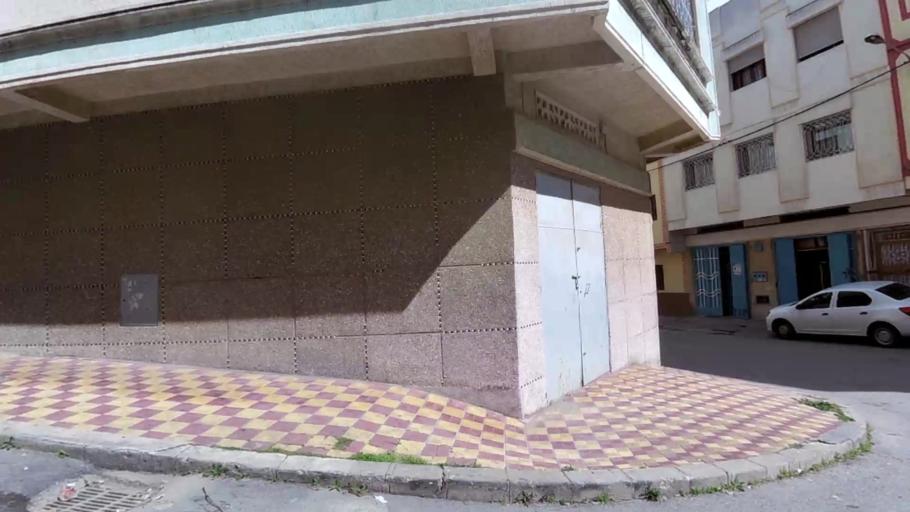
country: MA
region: Tanger-Tetouan
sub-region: Tanger-Assilah
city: Tangier
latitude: 35.7528
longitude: -5.8023
